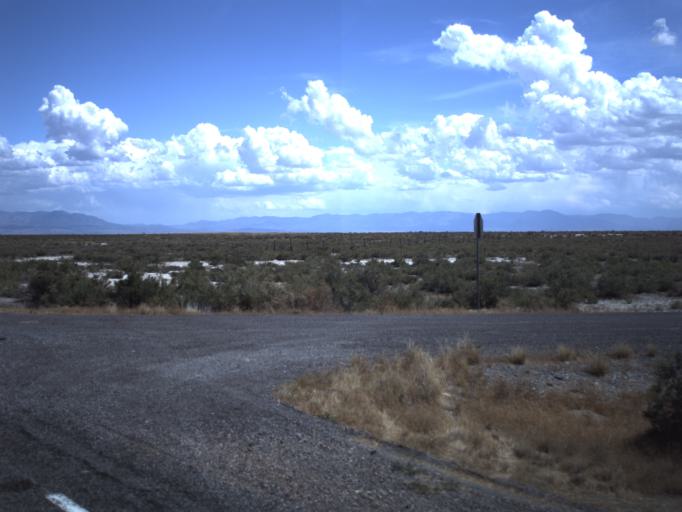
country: US
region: Utah
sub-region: Millard County
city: Delta
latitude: 39.3125
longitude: -112.7650
